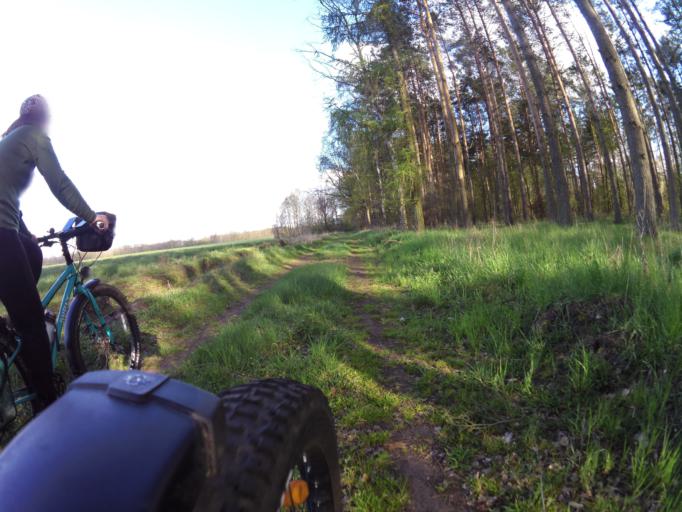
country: PL
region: West Pomeranian Voivodeship
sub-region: Powiat gryficki
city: Ploty
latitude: 53.7669
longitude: 15.2572
